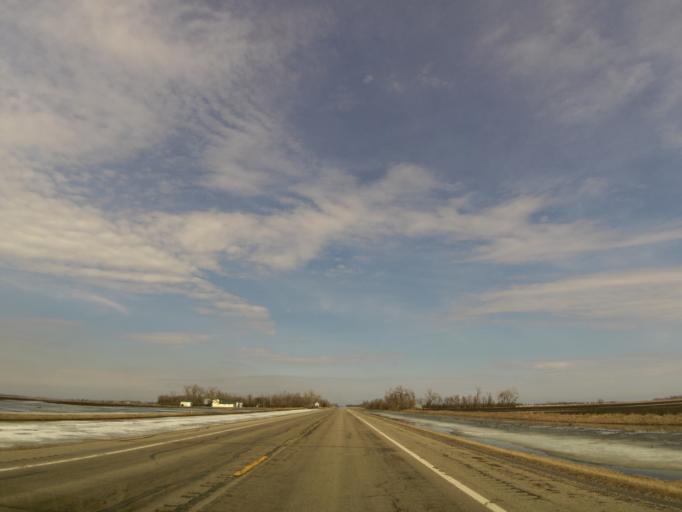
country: US
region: North Dakota
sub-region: Walsh County
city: Grafton
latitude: 48.3345
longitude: -97.4050
